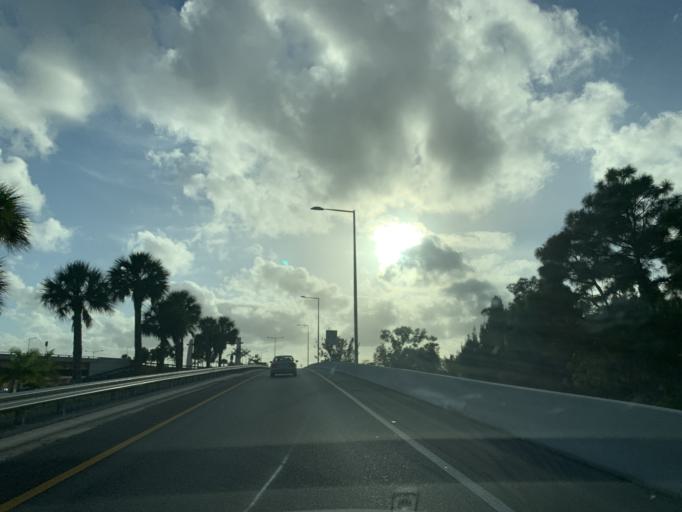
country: US
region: Florida
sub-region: Miami-Dade County
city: Sunset
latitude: 25.6970
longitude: -80.3429
